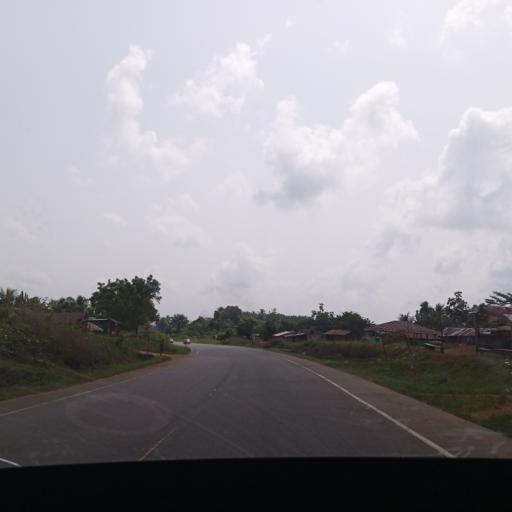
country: LR
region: Margibi
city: Kakata
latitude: 6.2355
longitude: -10.2829
